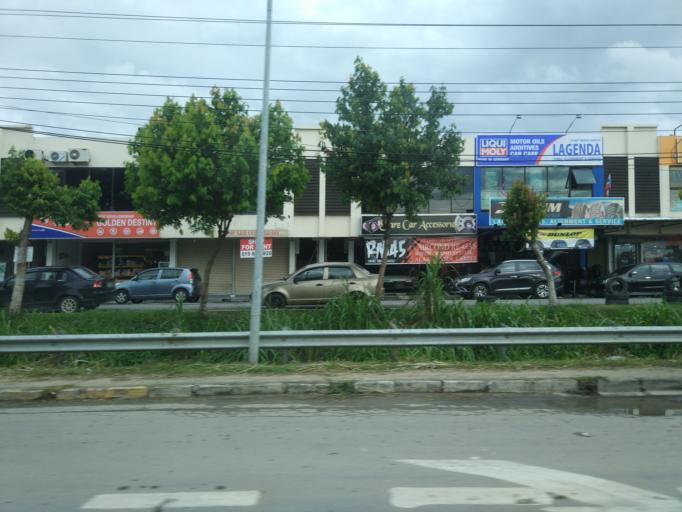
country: MY
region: Sabah
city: Kota Kinabalu
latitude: 6.0908
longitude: 116.1962
